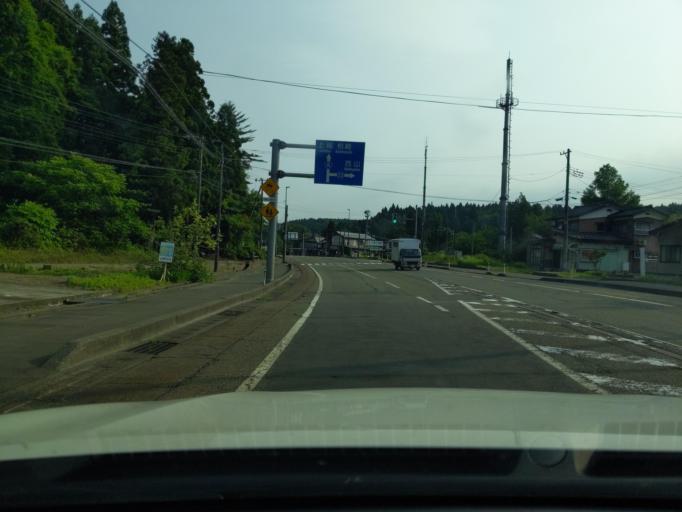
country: JP
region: Niigata
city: Nagaoka
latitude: 37.4346
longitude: 138.7291
